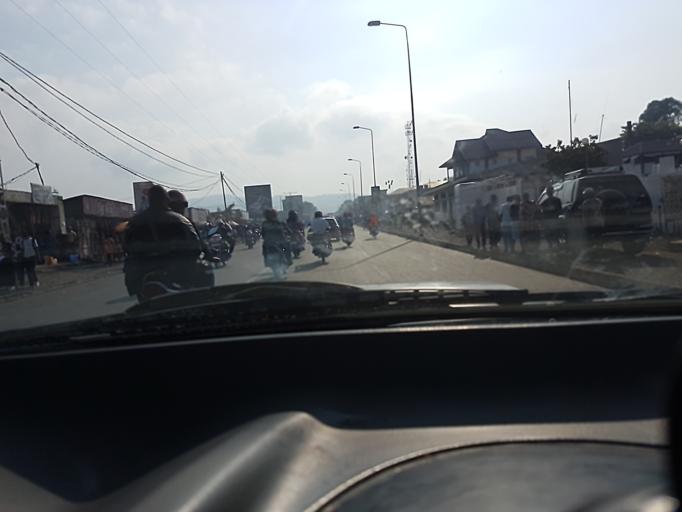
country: CD
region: Nord Kivu
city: Goma
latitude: -1.6785
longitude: 29.2250
